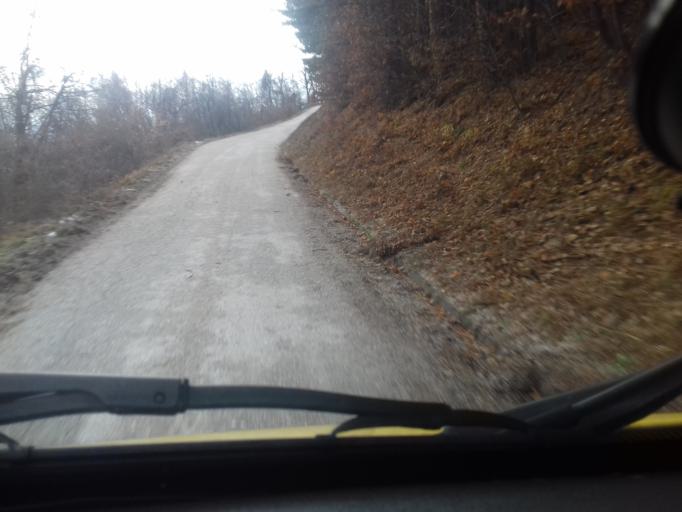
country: BA
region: Federation of Bosnia and Herzegovina
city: Zenica
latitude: 44.2280
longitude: 17.9630
